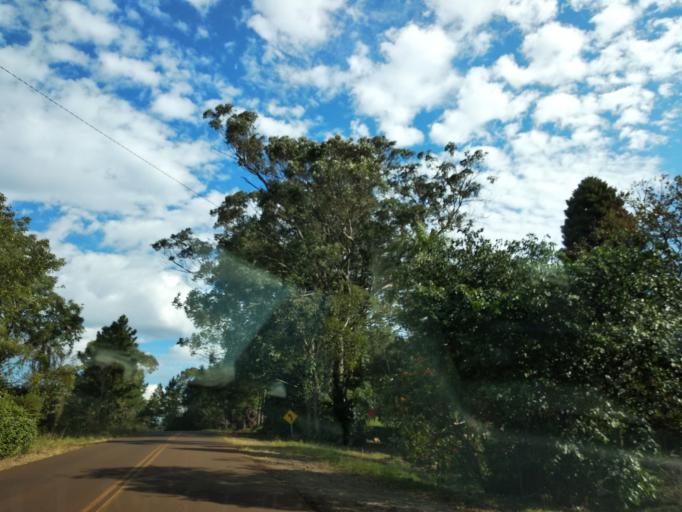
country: AR
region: Misiones
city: Aristobulo del Valle
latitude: -27.0729
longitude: -54.8313
